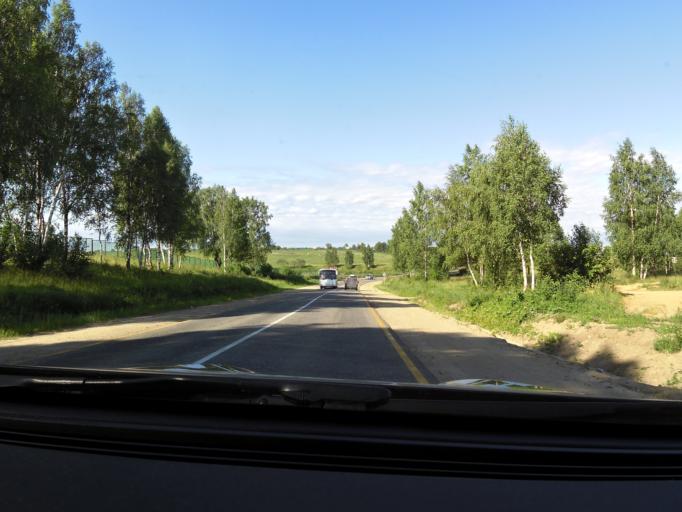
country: RU
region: Tverskaya
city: Zavidovo
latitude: 56.5816
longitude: 36.5337
